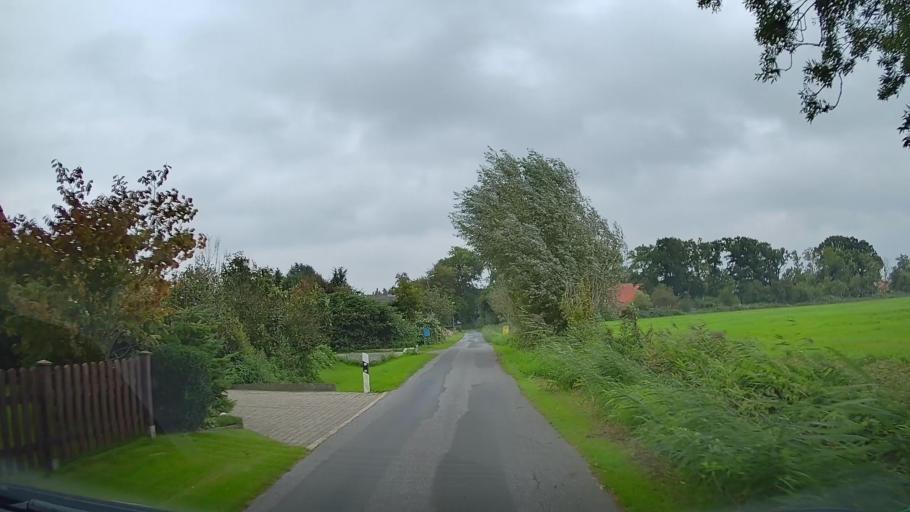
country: DE
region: Lower Saxony
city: Freiburg
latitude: 53.8272
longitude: 9.2635
